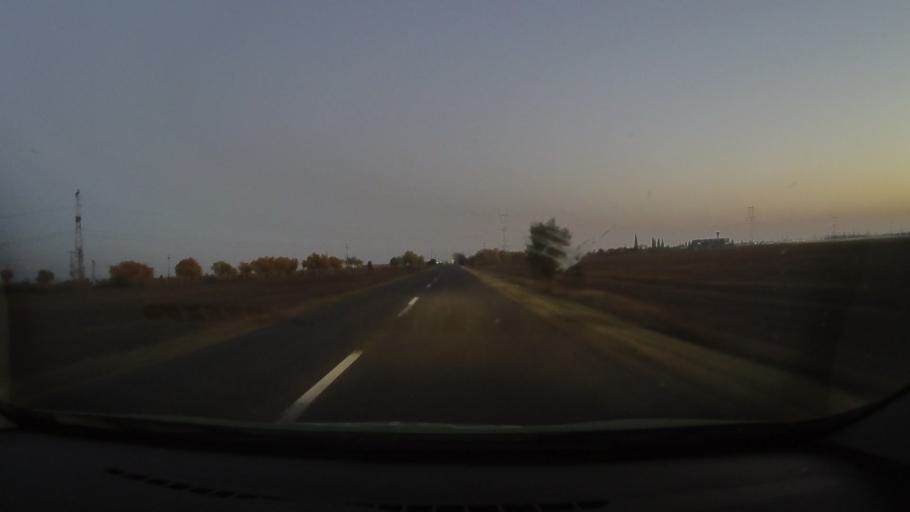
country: RO
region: Arad
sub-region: Comuna Livada
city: Livada
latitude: 46.1957
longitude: 21.3893
